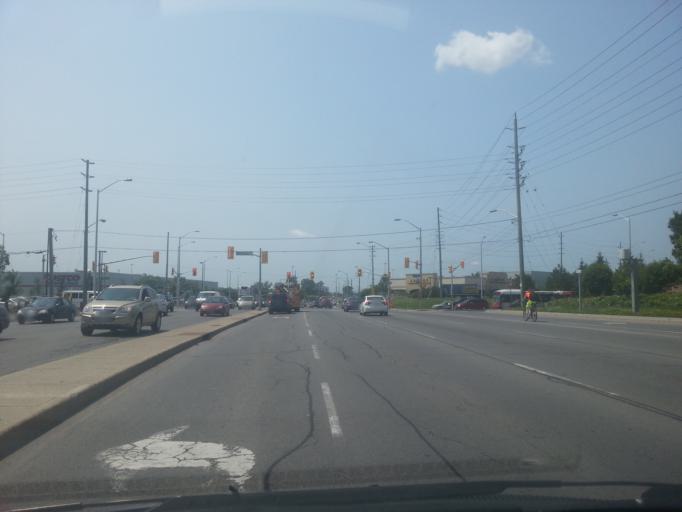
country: CA
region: Ontario
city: Ottawa
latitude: 45.4169
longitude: -75.6016
